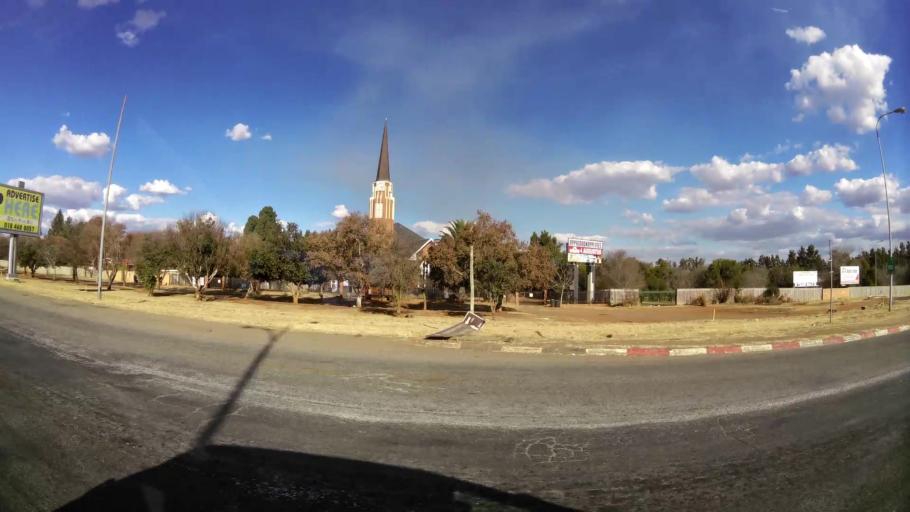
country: ZA
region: North-West
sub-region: Dr Kenneth Kaunda District Municipality
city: Klerksdorp
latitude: -26.8583
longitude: 26.6726
